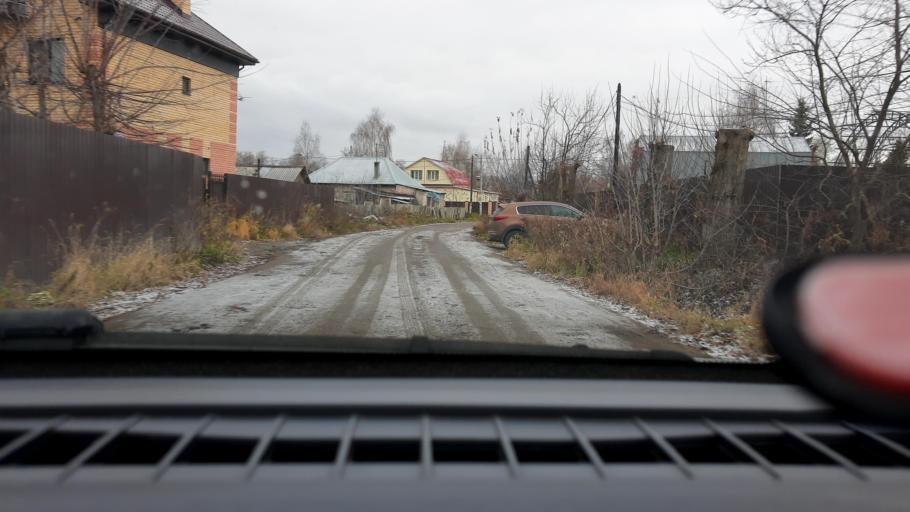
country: RU
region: Nizjnij Novgorod
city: Burevestnik
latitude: 56.2037
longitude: 43.7926
